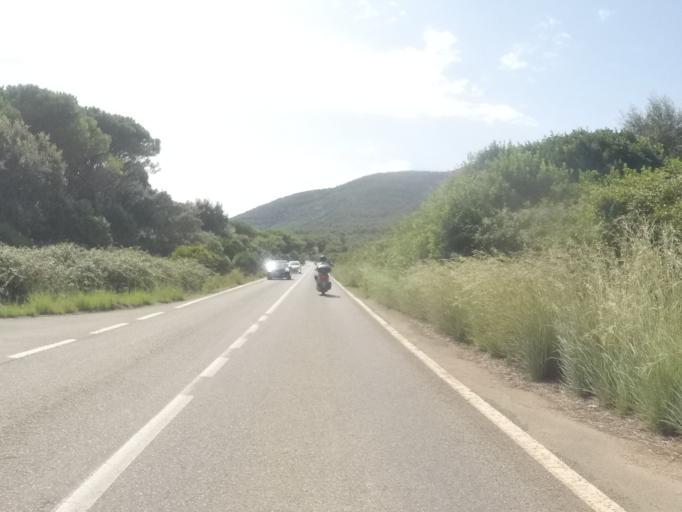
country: IT
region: Sardinia
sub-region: Provincia di Sassari
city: Alghero
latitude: 40.6187
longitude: 8.1908
